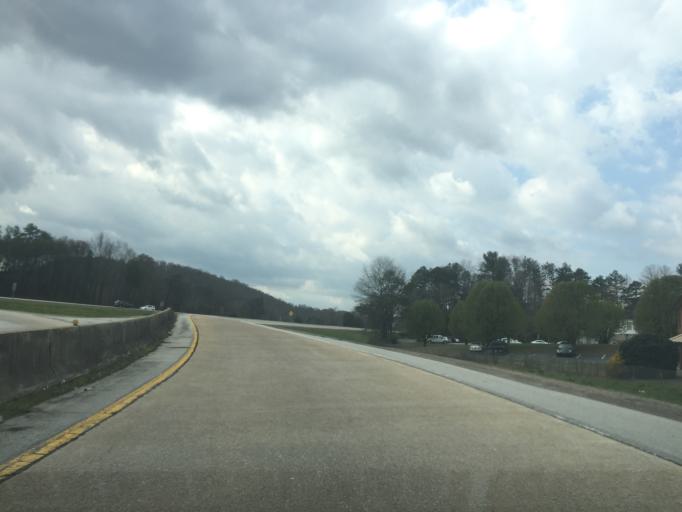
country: US
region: Tennessee
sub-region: Hamilton County
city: Falling Water
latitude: 35.1889
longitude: -85.2480
